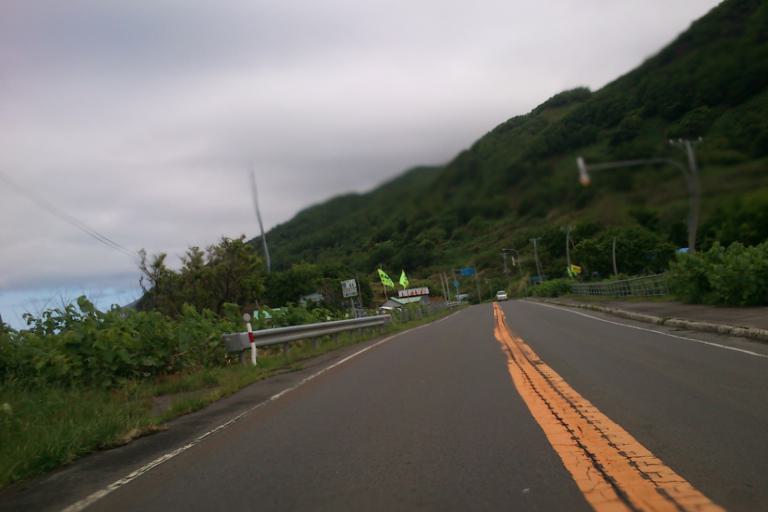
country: JP
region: Hokkaido
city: Ishikari
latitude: 43.4183
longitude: 141.4296
